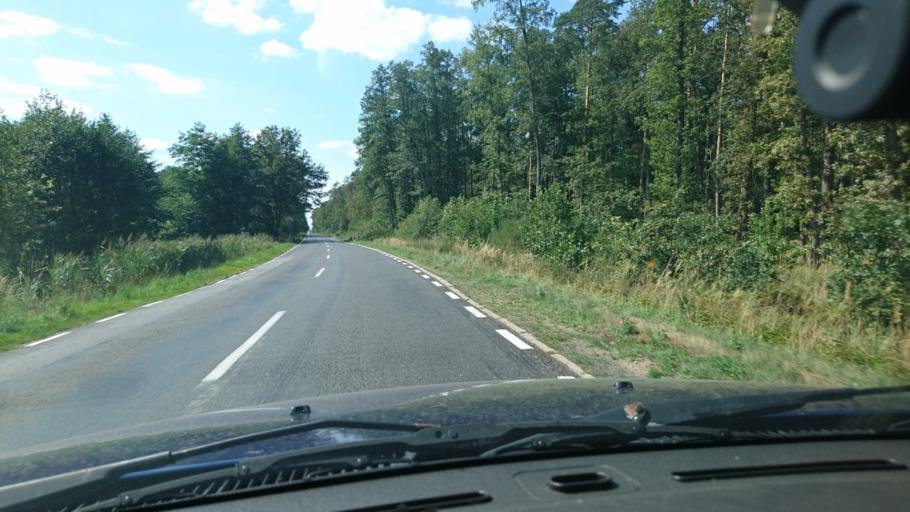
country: PL
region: Greater Poland Voivodeship
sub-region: Powiat krotoszynski
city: Sulmierzyce
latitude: 51.6017
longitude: 17.5887
